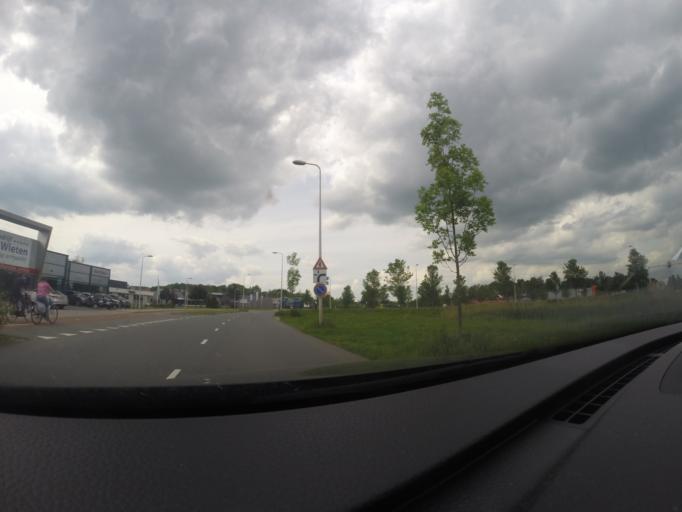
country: NL
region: Gelderland
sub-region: Gemeente Hattem
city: Hattem
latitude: 52.5121
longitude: 6.0504
